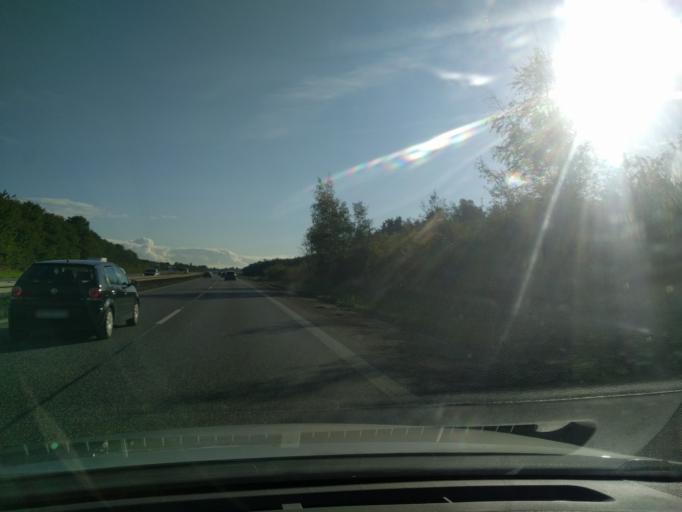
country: DK
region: Zealand
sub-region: Soro Kommune
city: Frederiksberg
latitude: 55.4525
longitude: 11.5988
